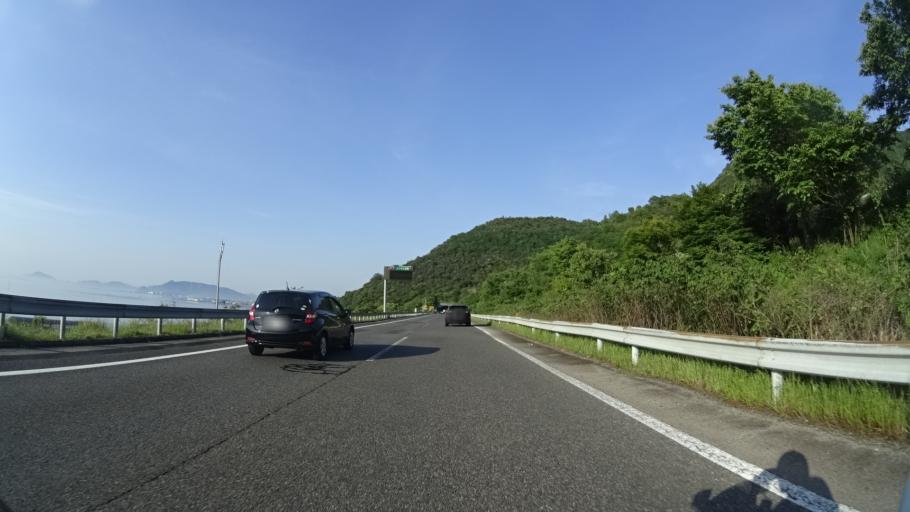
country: JP
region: Ehime
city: Kawanoecho
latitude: 34.0441
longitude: 133.6189
